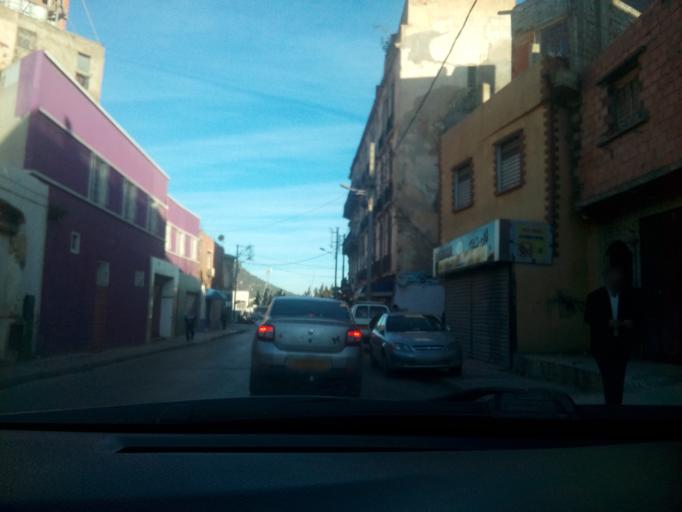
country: DZ
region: Oran
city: Oran
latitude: 35.6909
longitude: -0.6552
